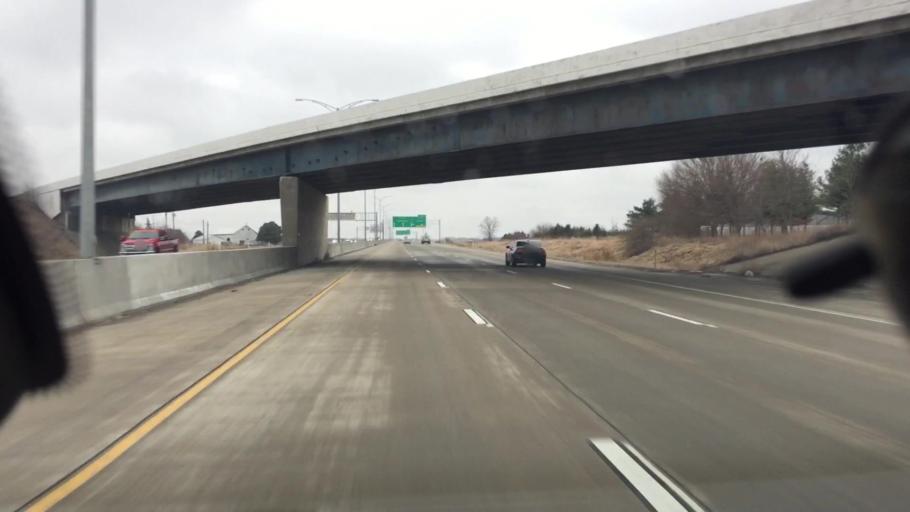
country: US
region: Illinois
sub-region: Tazewell County
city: Morton
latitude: 40.6268
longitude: -89.5016
